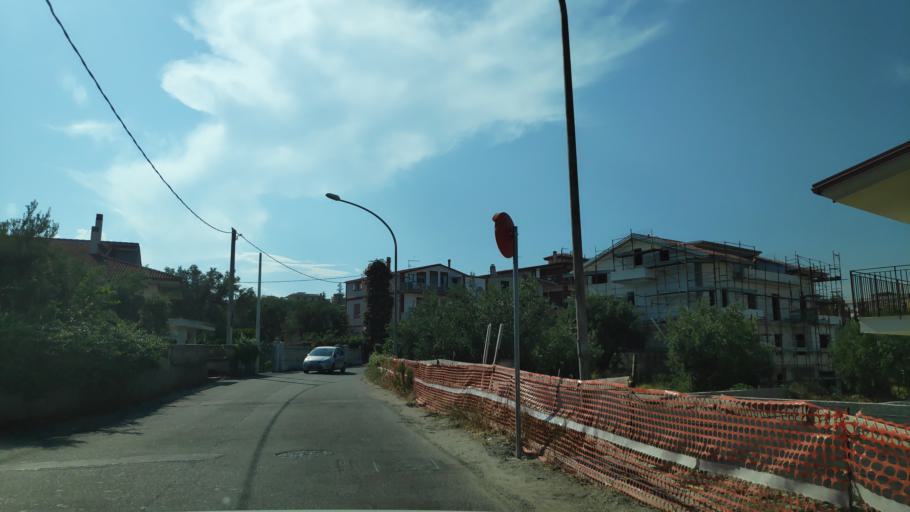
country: IT
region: Calabria
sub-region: Provincia di Catanzaro
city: Soverato Superiore
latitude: 38.6877
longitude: 16.5356
